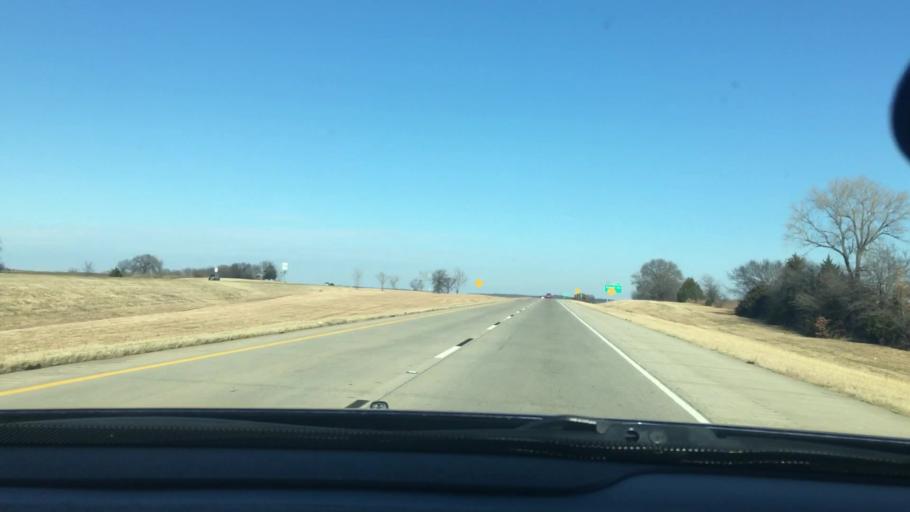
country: US
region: Oklahoma
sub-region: Love County
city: Marietta
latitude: 34.0202
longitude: -97.1453
